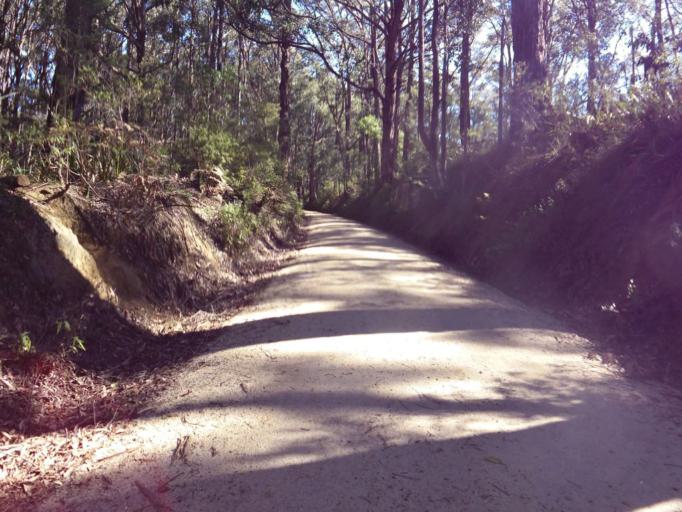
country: AU
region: Victoria
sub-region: Latrobe
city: Moe
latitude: -38.3907
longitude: 146.1821
